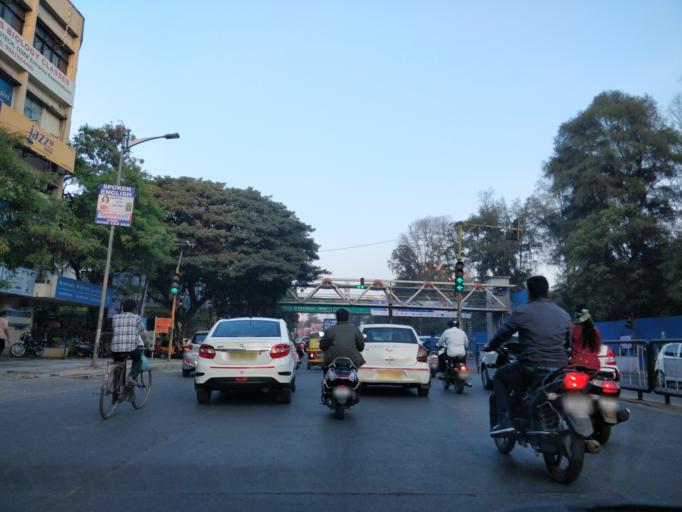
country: IN
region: Maharashtra
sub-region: Pune Division
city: Pune
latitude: 18.5027
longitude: 73.8180
